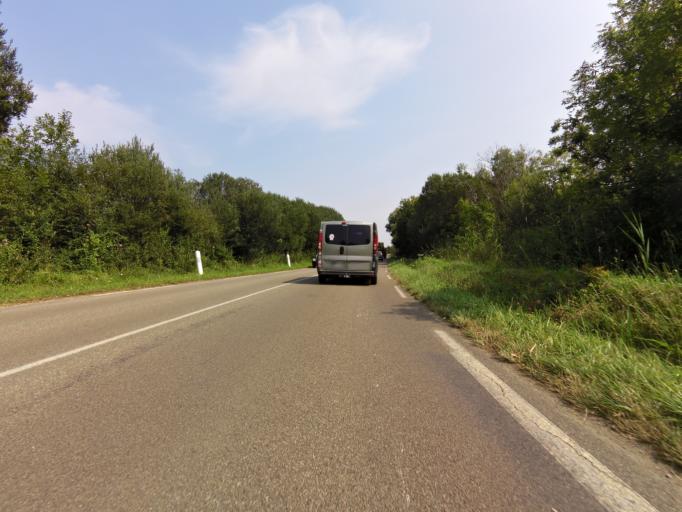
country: FR
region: Brittany
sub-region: Departement du Finistere
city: Esquibien
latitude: 48.0308
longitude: -4.5939
